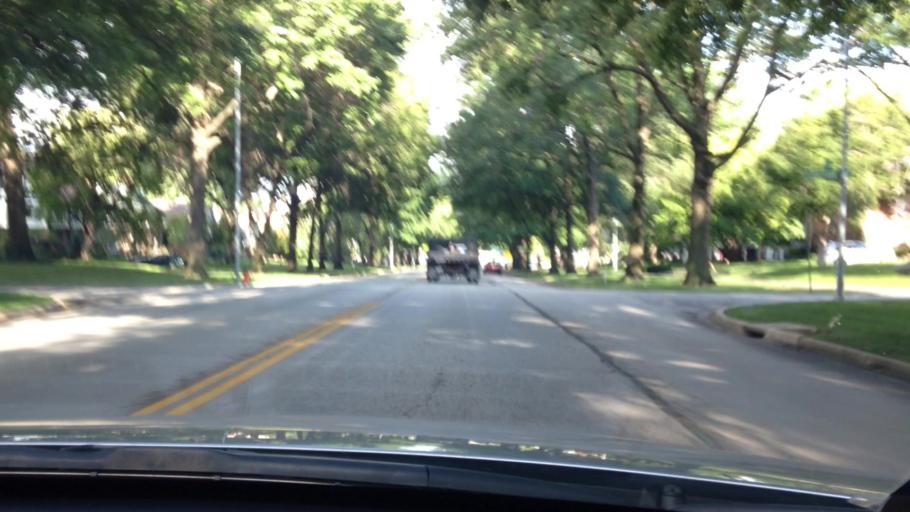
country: US
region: Kansas
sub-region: Johnson County
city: Mission Hills
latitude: 39.0123
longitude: -94.5964
